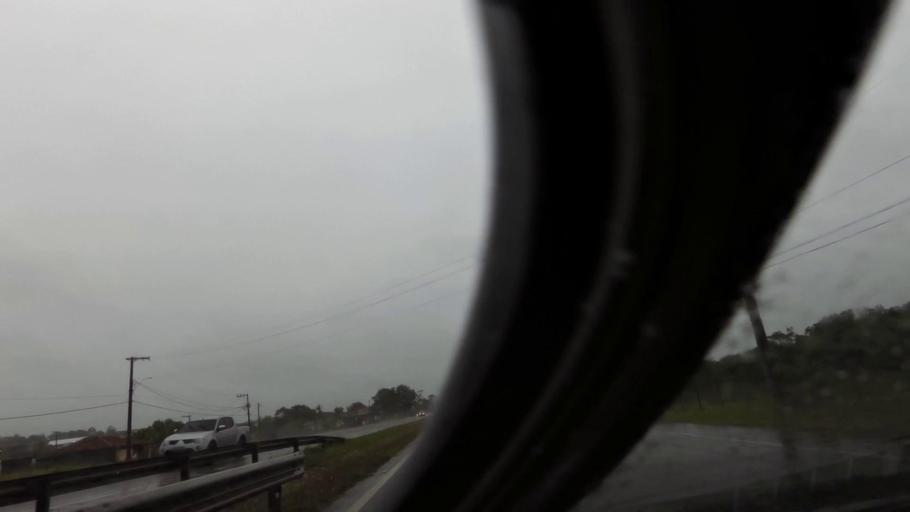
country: BR
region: Espirito Santo
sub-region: Guarapari
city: Guarapari
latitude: -20.5489
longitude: -40.3978
